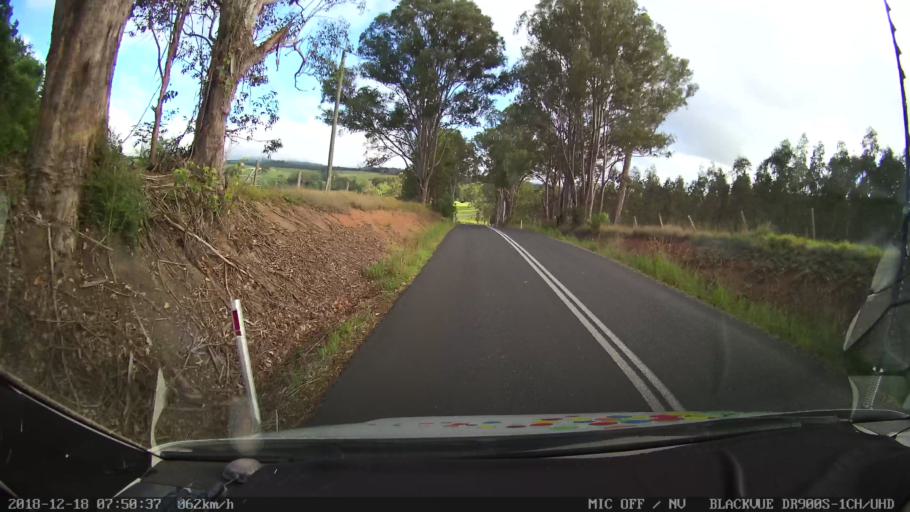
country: AU
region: New South Wales
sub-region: Kyogle
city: Kyogle
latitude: -28.4440
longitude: 152.5745
